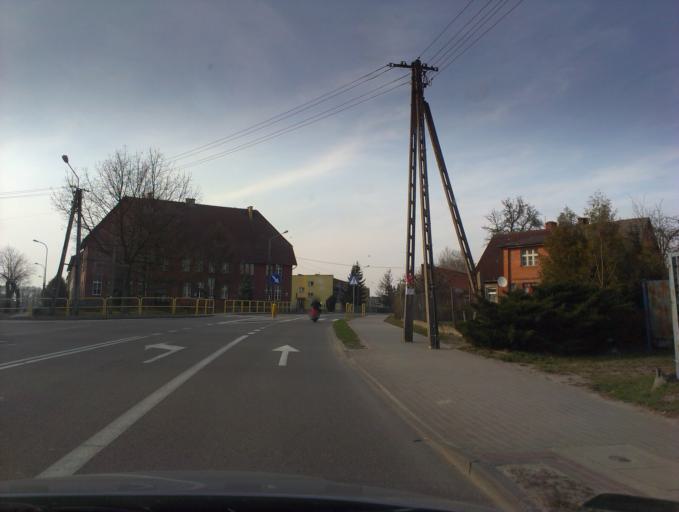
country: PL
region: Pomeranian Voivodeship
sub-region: Powiat czluchowski
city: Debrzno
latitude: 53.5415
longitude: 17.2348
